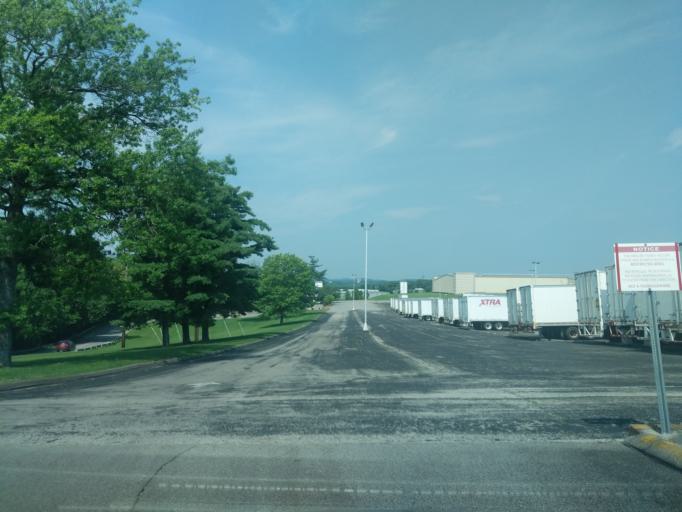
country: US
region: Tennessee
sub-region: Davidson County
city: Lakewood
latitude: 36.2670
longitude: -86.6528
